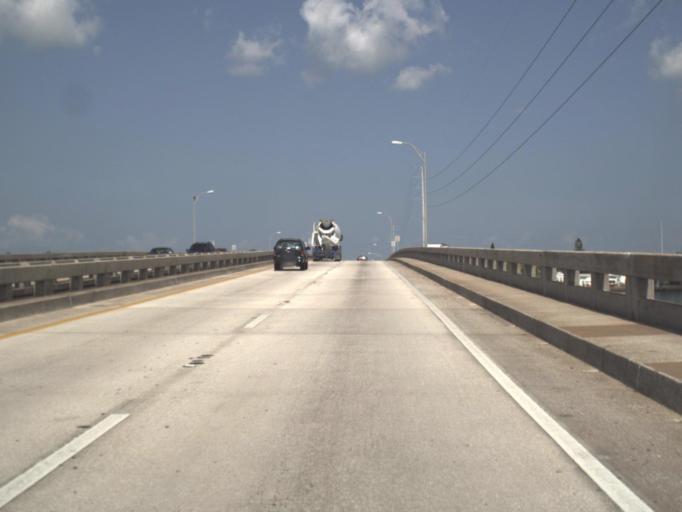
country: US
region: Florida
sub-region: Pinellas County
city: Bay Pines
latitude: 27.8129
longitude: -82.7628
